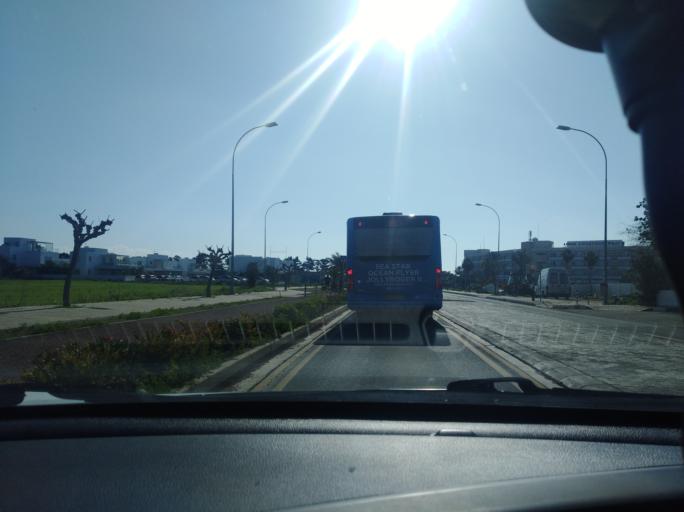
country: CY
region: Pafos
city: Paphos
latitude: 34.7388
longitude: 32.4369
